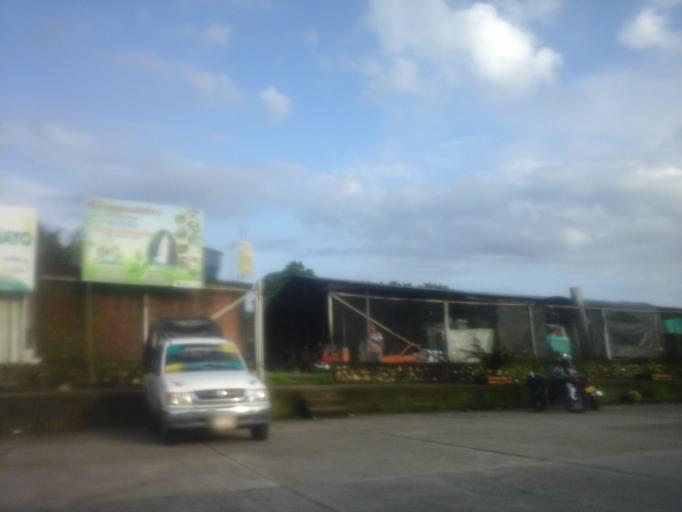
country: CO
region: Putumayo
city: Orito
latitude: 0.6668
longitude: -76.8736
